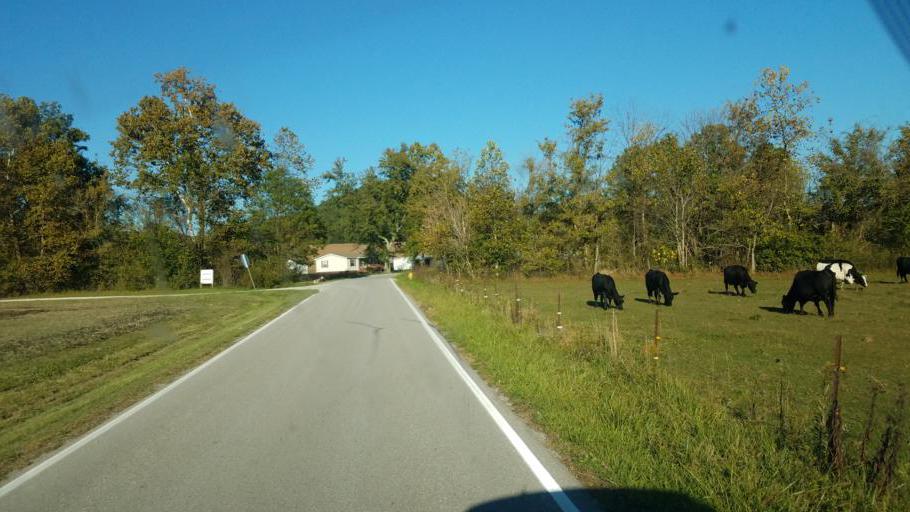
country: US
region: Ohio
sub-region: Adams County
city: Manchester
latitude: 38.5090
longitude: -83.5420
